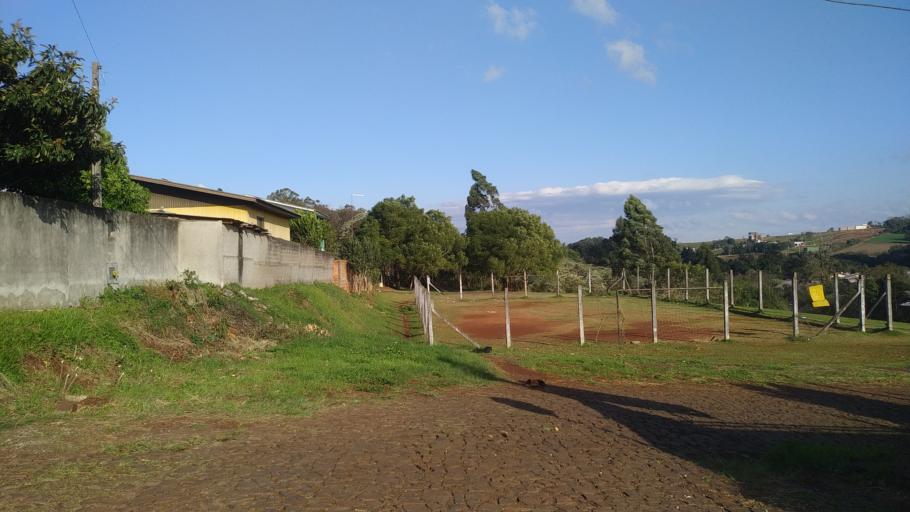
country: BR
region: Santa Catarina
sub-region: Chapeco
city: Chapeco
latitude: -27.0669
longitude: -52.6091
